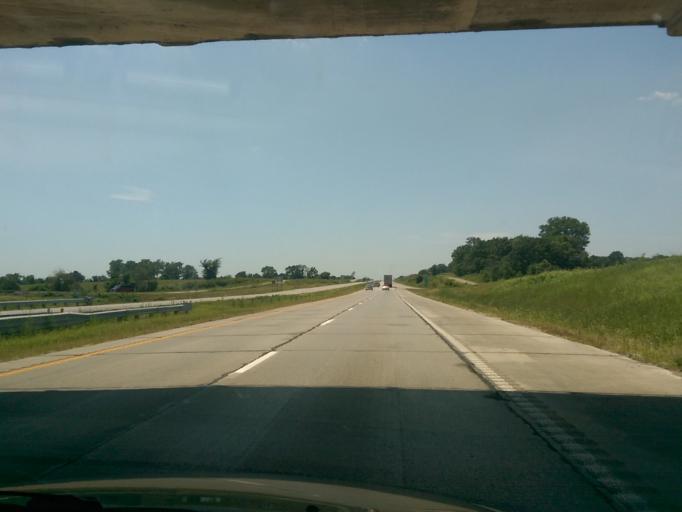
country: US
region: Missouri
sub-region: Saline County
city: Sweet Springs
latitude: 38.9716
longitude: -93.2717
